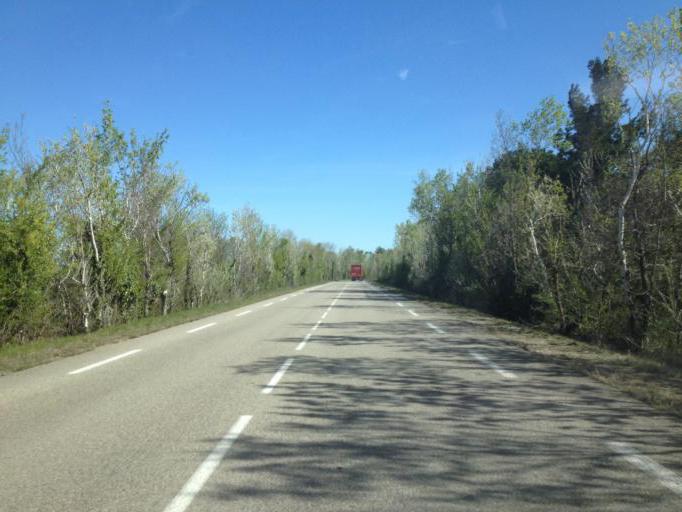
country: FR
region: Provence-Alpes-Cote d'Azur
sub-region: Departement du Vaucluse
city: Caderousse
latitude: 44.1265
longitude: 4.7203
